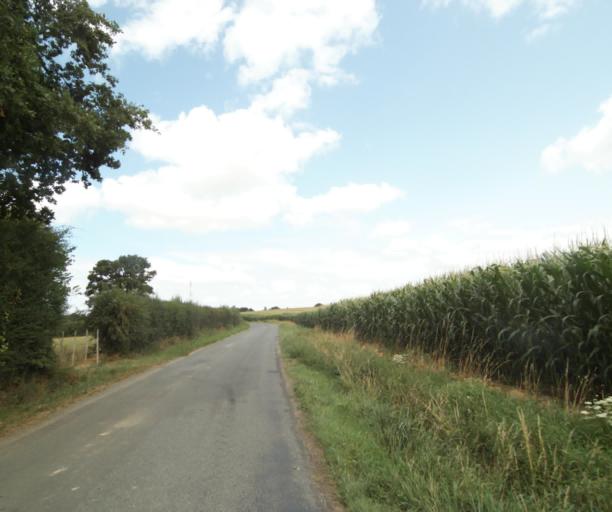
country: FR
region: Pays de la Loire
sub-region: Departement de la Sarthe
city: Sable-sur-Sarthe
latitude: 47.8609
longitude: -0.3569
